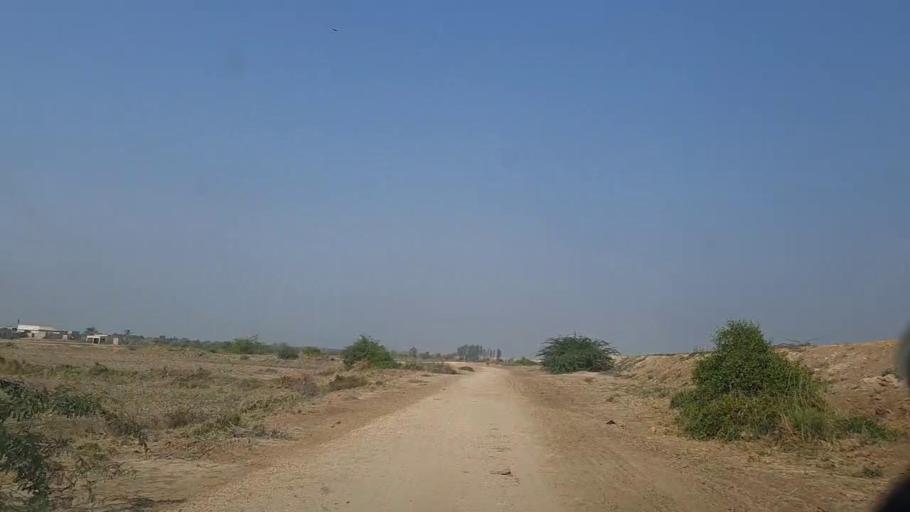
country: PK
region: Sindh
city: Thatta
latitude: 24.6636
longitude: 67.9254
